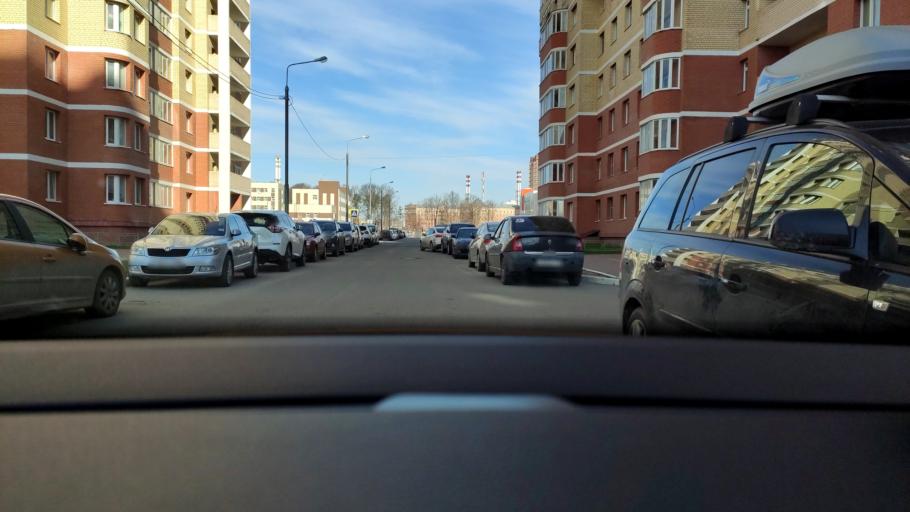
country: RU
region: Moskovskaya
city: Reutov
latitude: 55.7757
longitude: 37.8936
